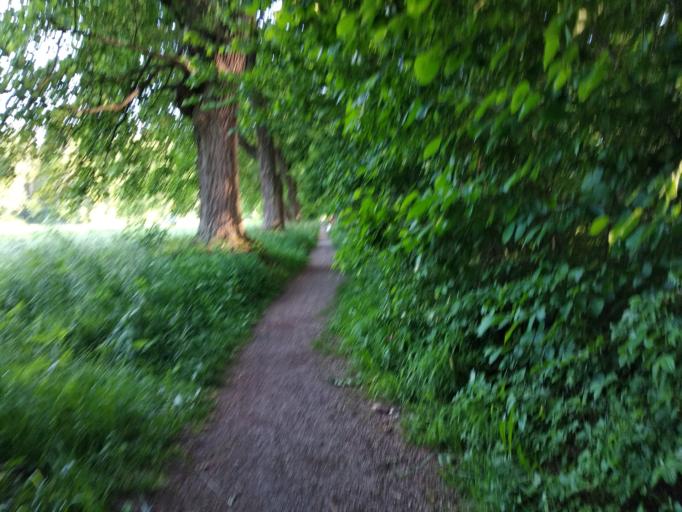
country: DE
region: Baden-Wuerttemberg
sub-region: Tuebingen Region
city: Aitrach
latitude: 47.9458
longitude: 10.1101
